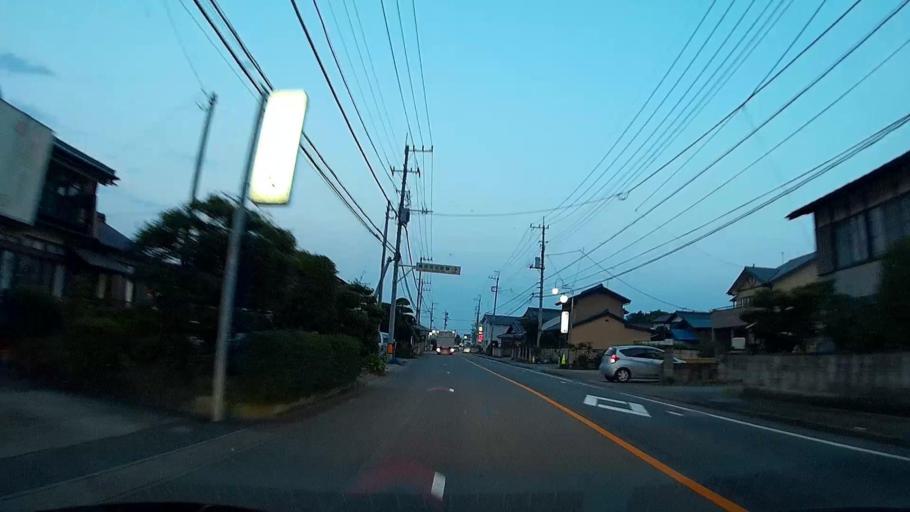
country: JP
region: Gunma
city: Annaka
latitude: 36.3765
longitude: 138.8917
